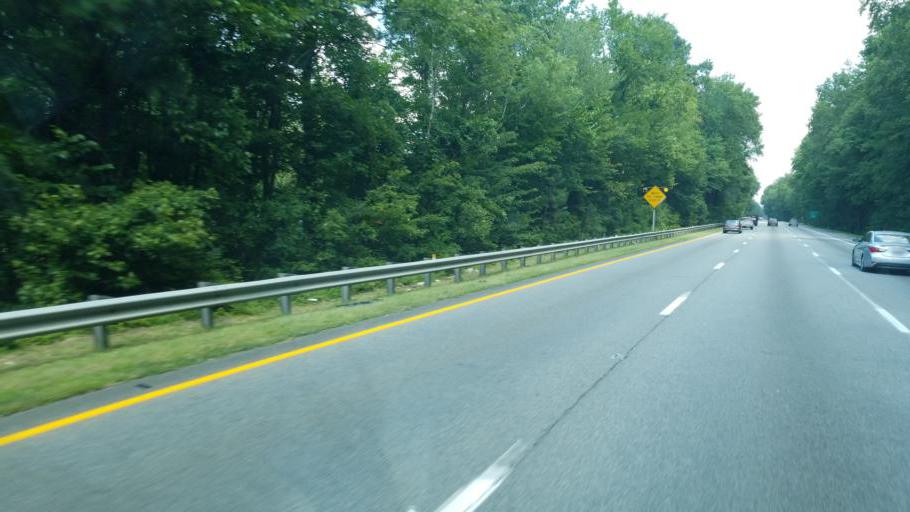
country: US
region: Virginia
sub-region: City of Suffolk
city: Suffolk
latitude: 36.7550
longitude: -76.5122
